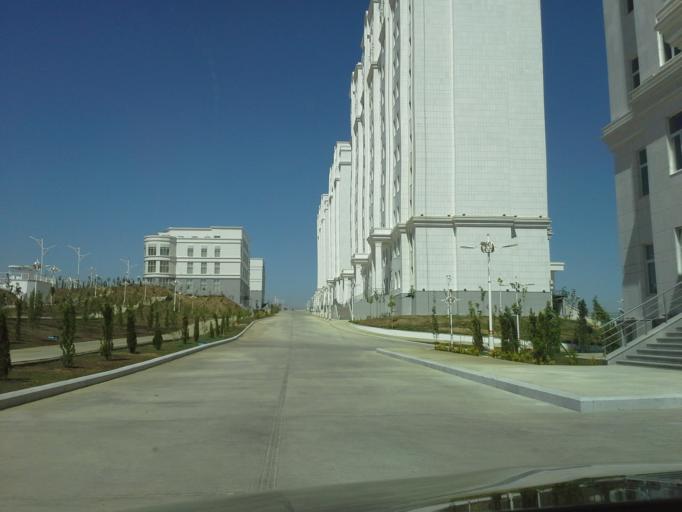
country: TM
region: Ahal
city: Ashgabat
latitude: 37.9420
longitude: 58.3505
